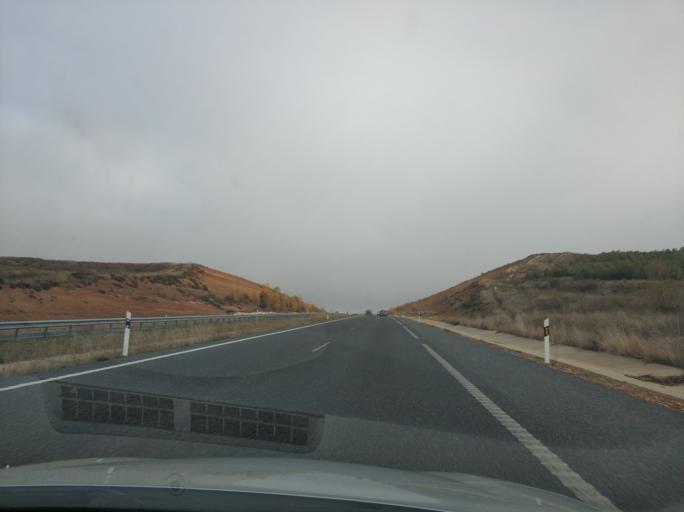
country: ES
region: Castille and Leon
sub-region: Provincia de Leon
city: Valdefresno
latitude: 42.5636
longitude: -5.5326
